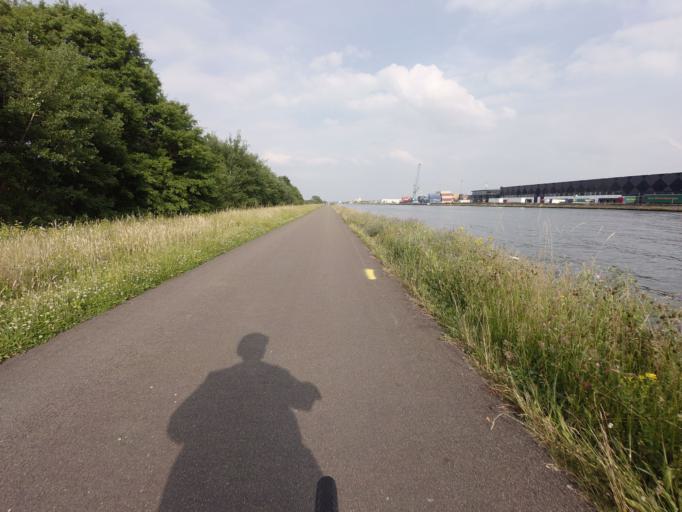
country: BE
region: Flanders
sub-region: Provincie Antwerpen
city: Grobbendonk
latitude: 51.1855
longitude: 4.6998
